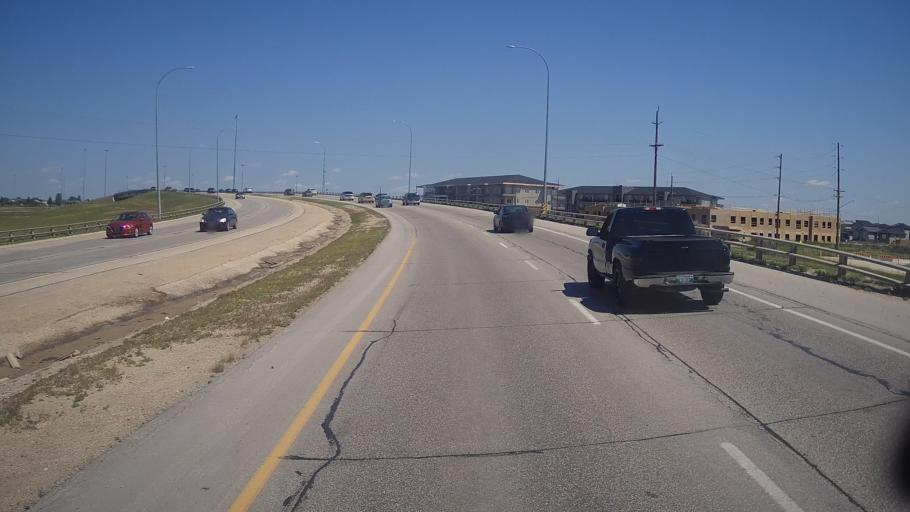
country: CA
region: Manitoba
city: Winnipeg
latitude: 49.9077
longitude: -97.0595
